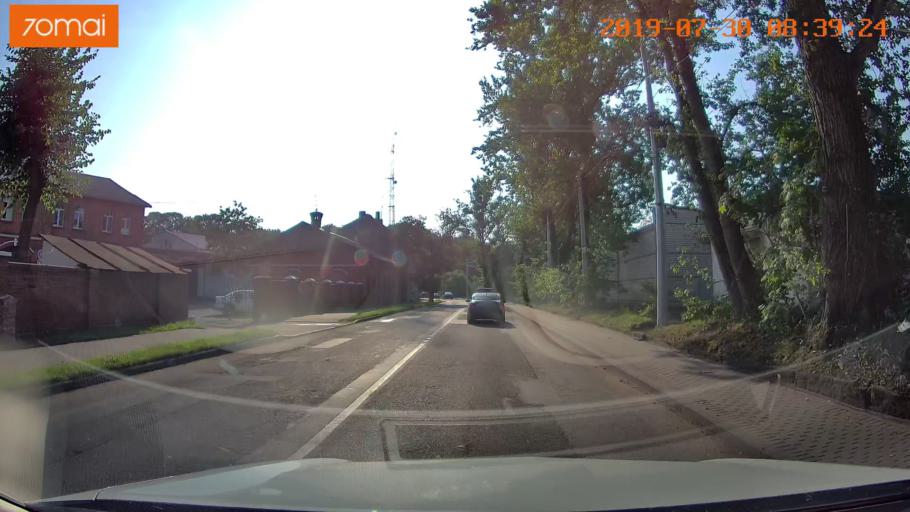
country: RU
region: Kaliningrad
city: Chernyakhovsk
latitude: 54.6311
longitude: 21.8035
